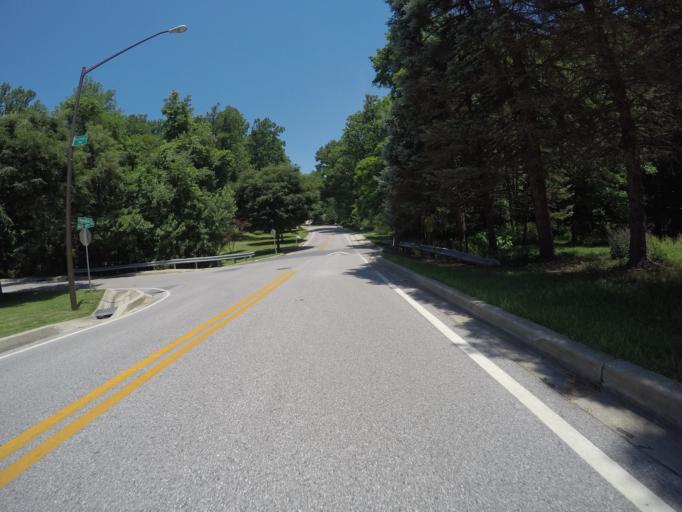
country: US
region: Maryland
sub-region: Howard County
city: Ilchester
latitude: 39.2391
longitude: -76.7864
